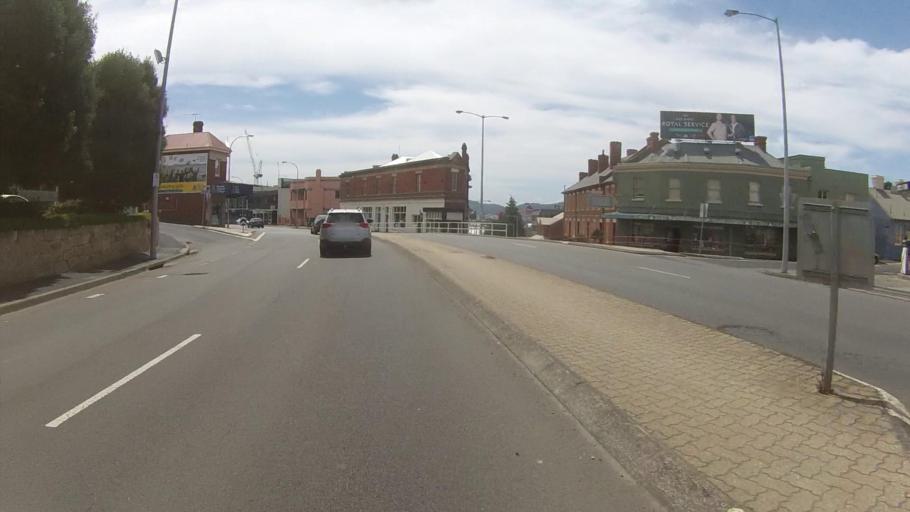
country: AU
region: Tasmania
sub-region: Hobart
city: Sandy Bay
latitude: -42.8896
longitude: 147.3302
